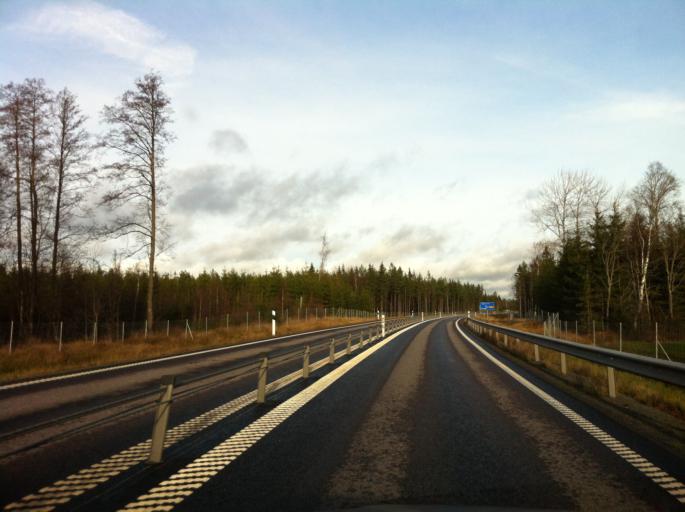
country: SE
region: Kronoberg
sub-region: Almhults Kommun
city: AElmhult
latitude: 56.6423
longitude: 14.2701
